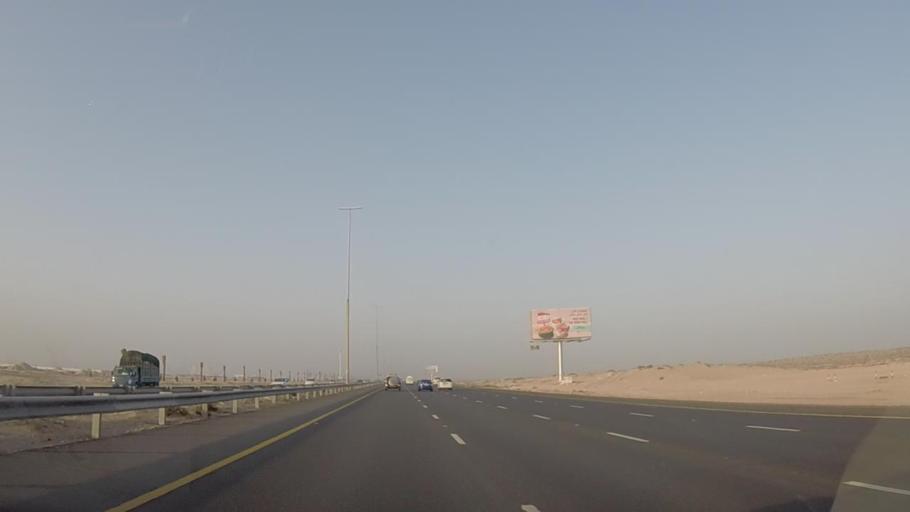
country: AE
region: Dubai
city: Dubai
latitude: 24.9315
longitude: 55.0173
